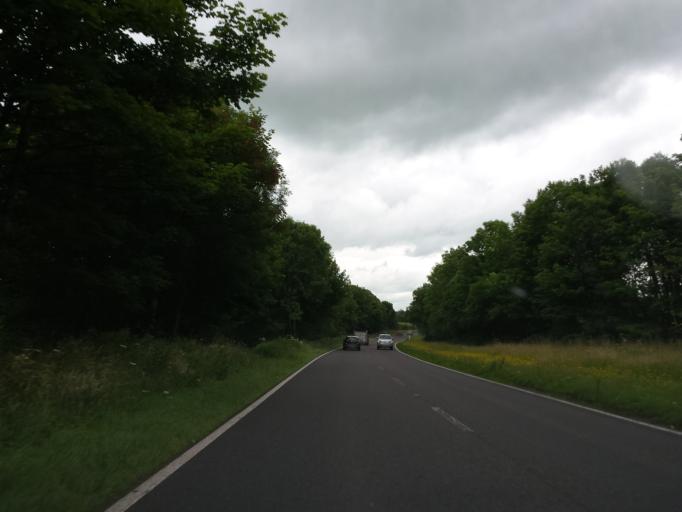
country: GB
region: Scotland
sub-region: Dumfries and Galloway
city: Dalbeattie
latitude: 55.0493
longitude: -3.7823
